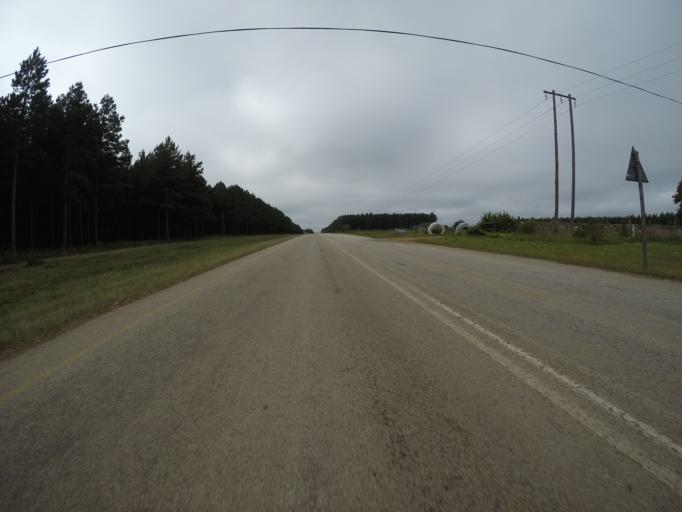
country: ZA
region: Eastern Cape
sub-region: Cacadu District Municipality
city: Kareedouw
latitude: -33.9951
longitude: 24.1257
